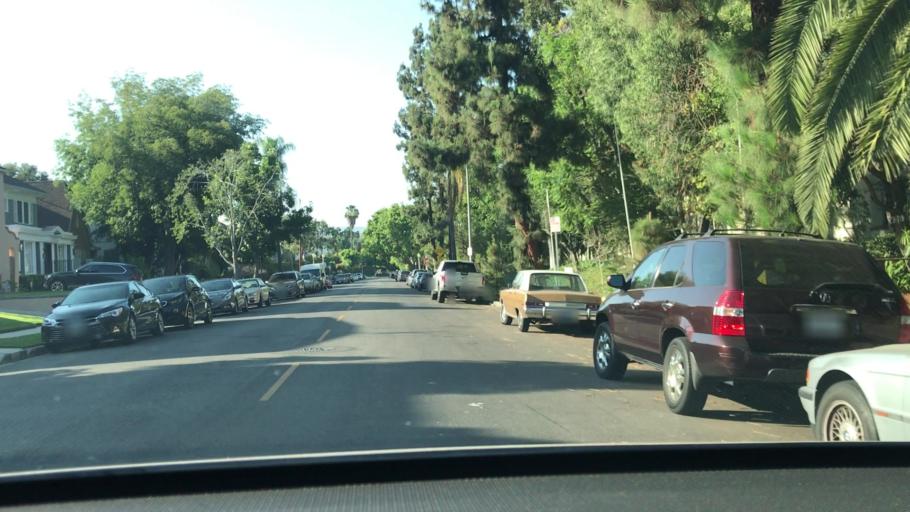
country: US
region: California
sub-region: Los Angeles County
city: Hollywood
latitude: 34.0660
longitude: -118.3173
